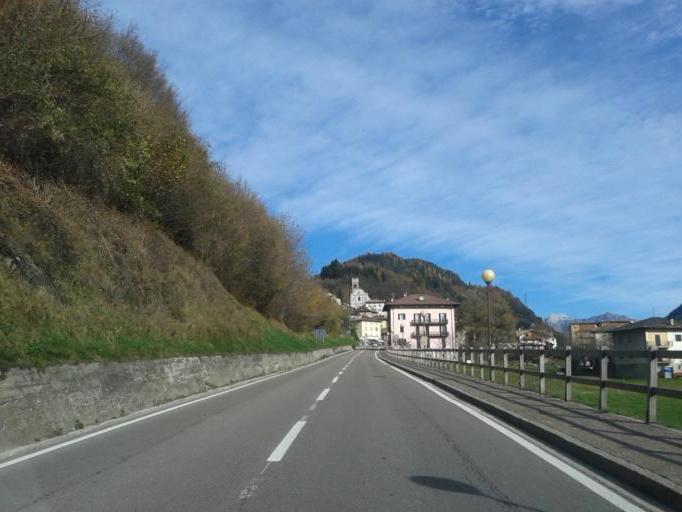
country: IT
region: Trentino-Alto Adige
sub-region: Provincia di Trento
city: Roncone
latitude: 45.9811
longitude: 10.6690
